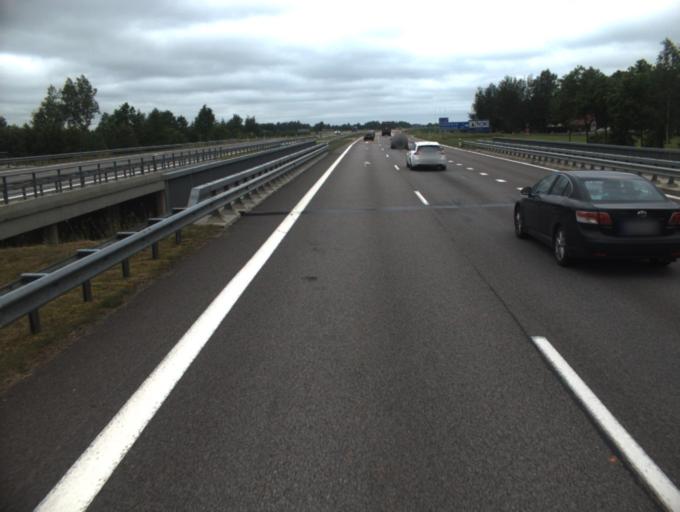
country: LT
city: Skaudvile
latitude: 55.4228
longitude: 22.7667
